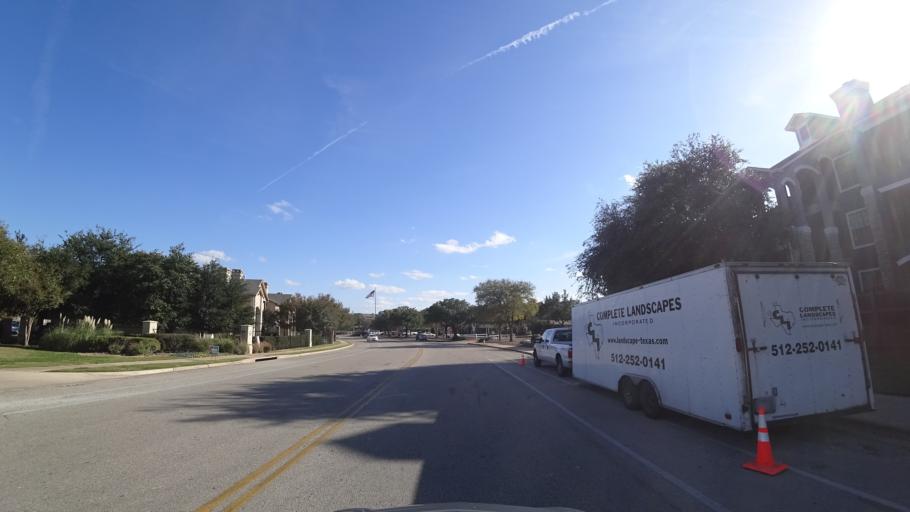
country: US
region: Texas
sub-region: Travis County
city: Wells Branch
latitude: 30.4558
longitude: -97.6856
